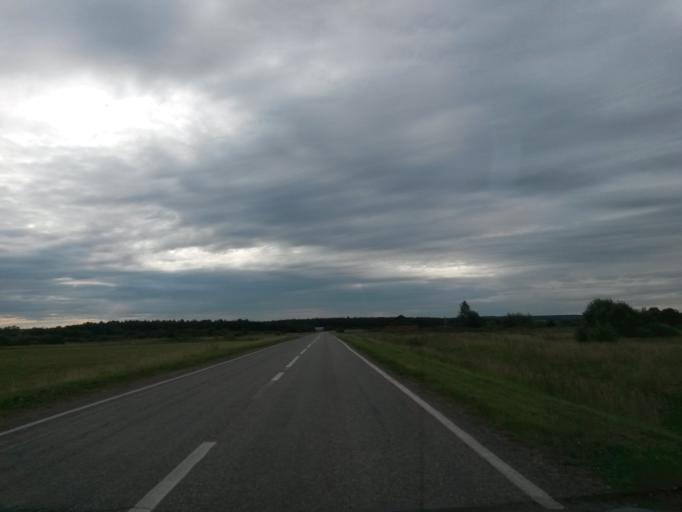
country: RU
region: Jaroslavl
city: Gavrilov-Yam
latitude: 57.3274
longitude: 39.8521
